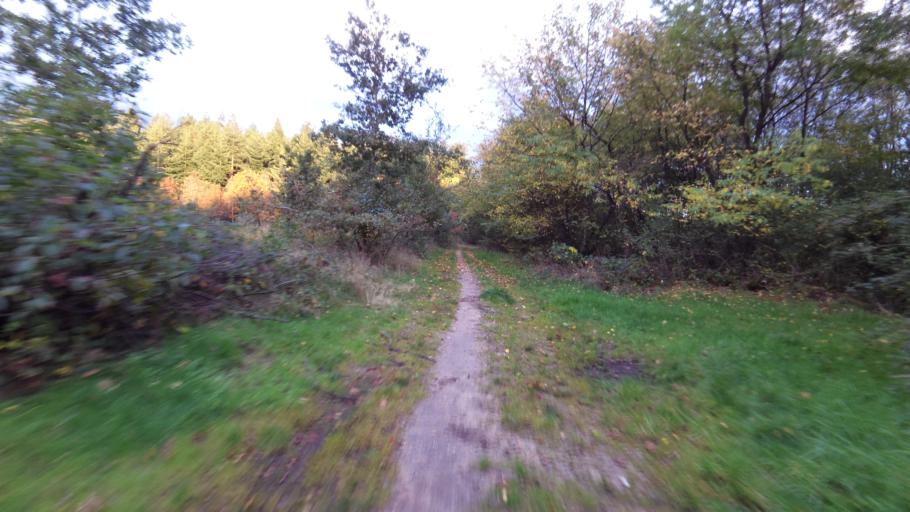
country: NL
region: Gelderland
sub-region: Gemeente Ede
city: Wekerom
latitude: 52.0823
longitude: 5.6849
